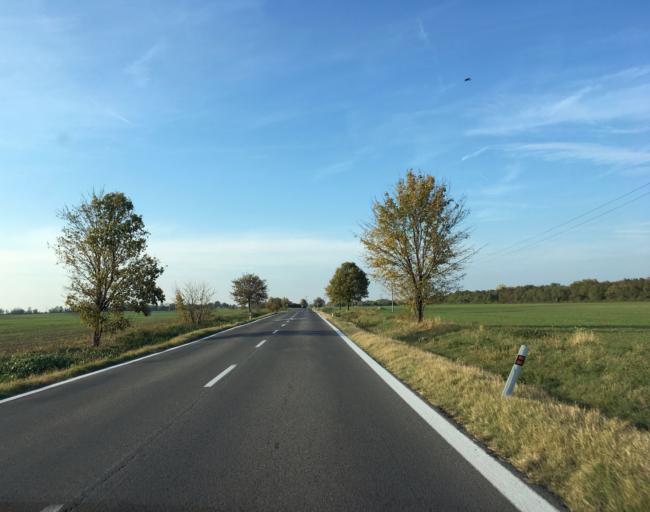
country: SK
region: Nitriansky
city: Surany
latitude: 48.0496
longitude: 18.1139
